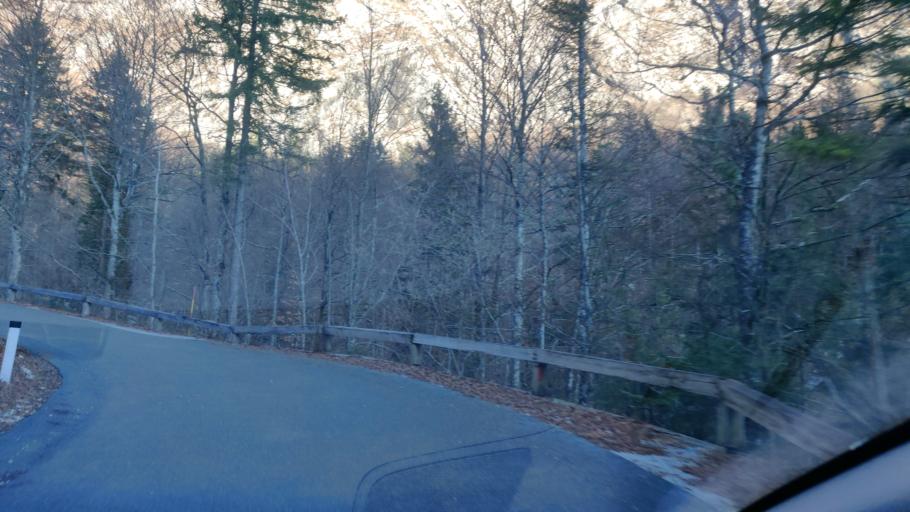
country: SI
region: Tolmin
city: Tolmin
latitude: 46.2890
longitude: 13.8070
